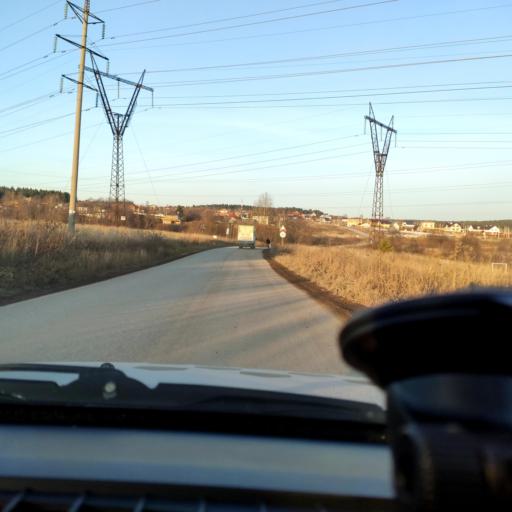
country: RU
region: Perm
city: Ferma
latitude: 57.9499
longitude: 56.3634
